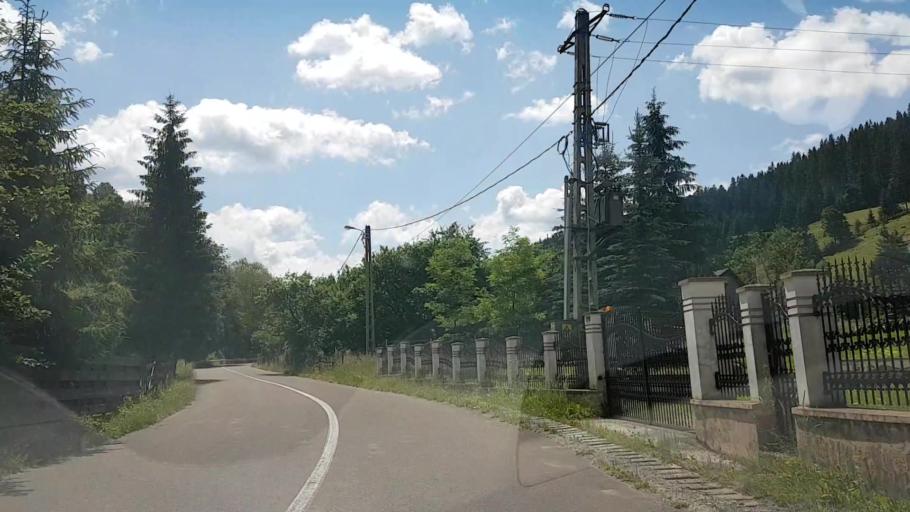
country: RO
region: Suceava
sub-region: Comuna Pojorata
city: Pojorata
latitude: 47.4934
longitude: 25.4840
